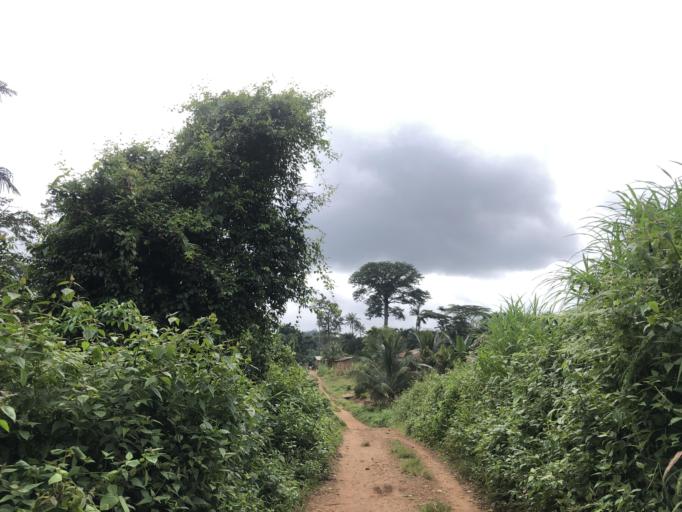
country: SL
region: Eastern Province
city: Kailahun
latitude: 8.2753
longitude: -10.5558
